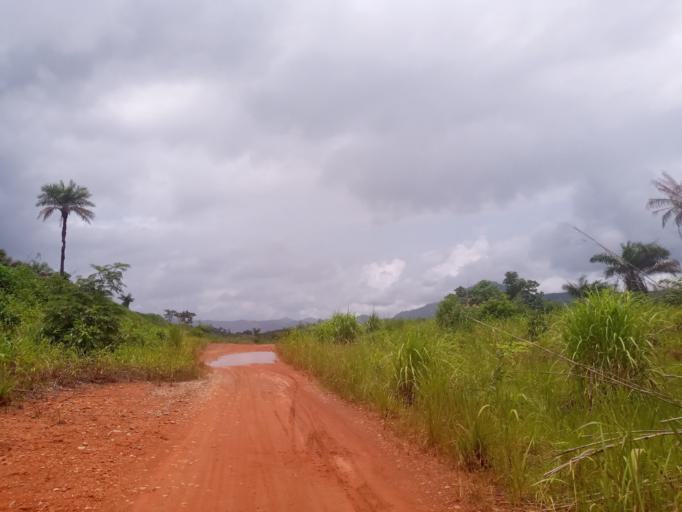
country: SL
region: Northern Province
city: Bumbuna
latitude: 8.9743
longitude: -11.7544
